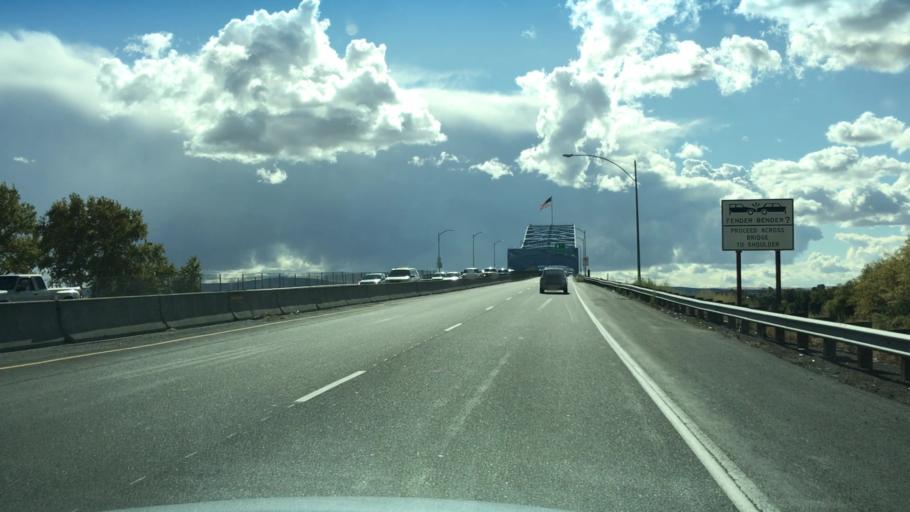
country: US
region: Washington
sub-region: Benton County
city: Kennewick
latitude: 46.2292
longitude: -119.1340
